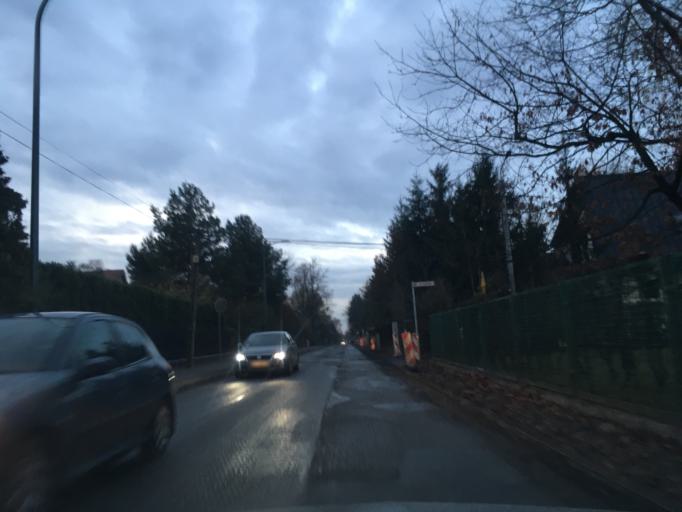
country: PL
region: Masovian Voivodeship
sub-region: Powiat piaseczynski
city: Piaseczno
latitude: 52.0556
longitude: 20.9839
